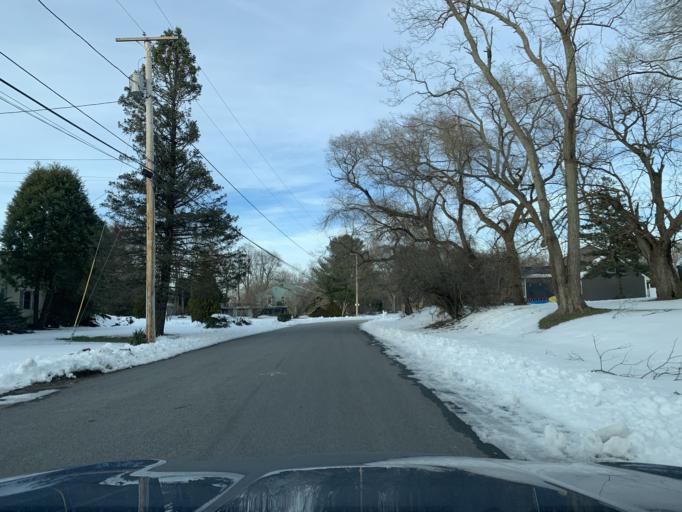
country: US
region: Rhode Island
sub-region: Washington County
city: North Kingstown
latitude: 41.5890
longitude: -71.4408
